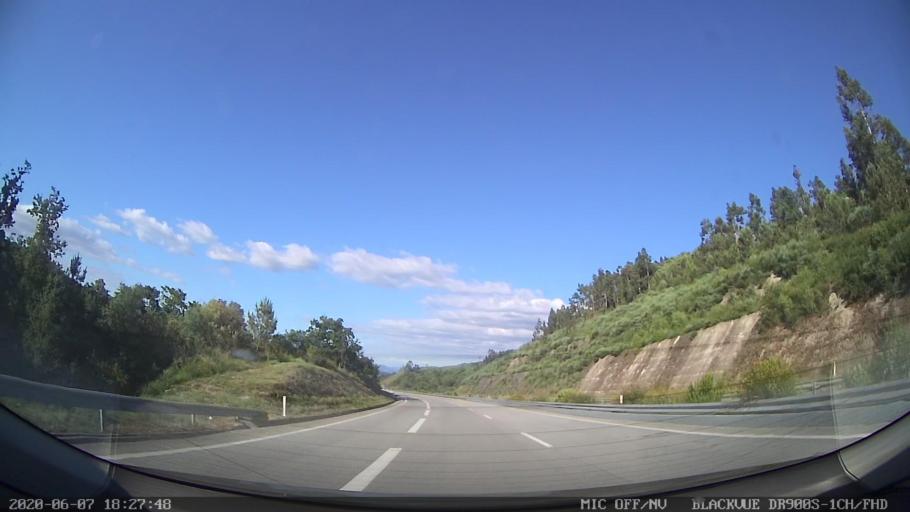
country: PT
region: Braga
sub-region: Celorico de Basto
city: Celorico de Basto
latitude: 41.4480
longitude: -8.0553
